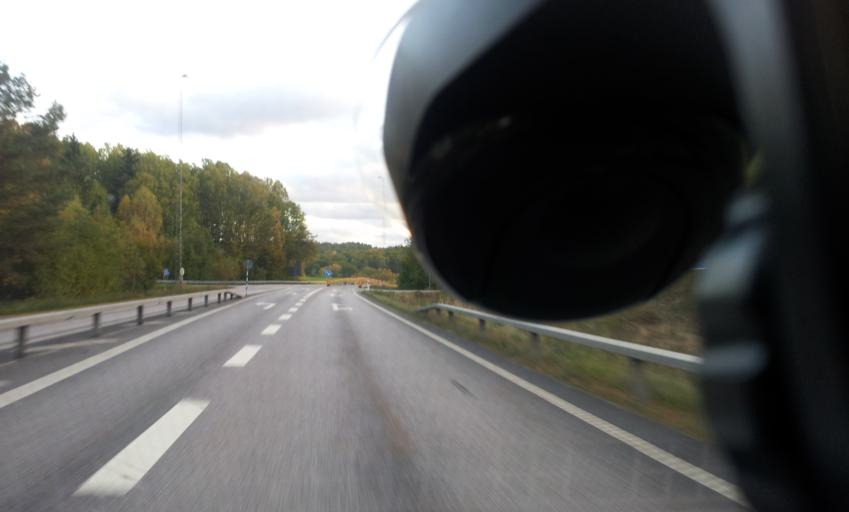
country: SE
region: Kalmar
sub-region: Vasterviks Kommun
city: Forserum
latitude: 58.0024
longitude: 16.4883
